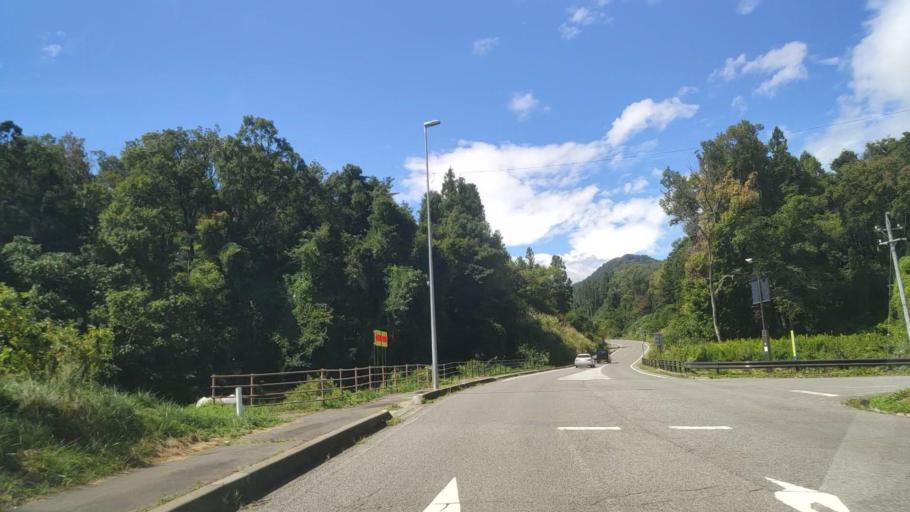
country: JP
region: Nagano
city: Suzaka
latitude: 36.7161
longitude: 138.2630
